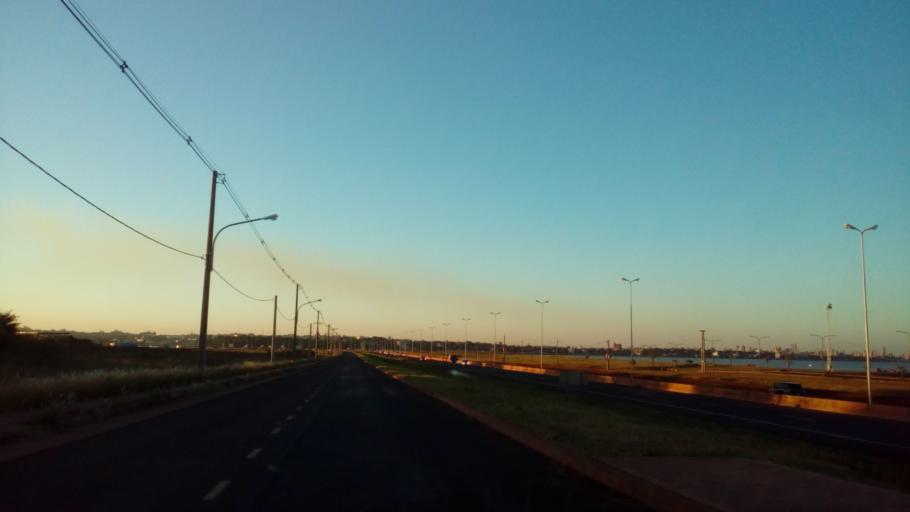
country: AR
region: Misiones
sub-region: Departamento de Capital
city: Posadas
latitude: -27.4203
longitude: -55.8799
